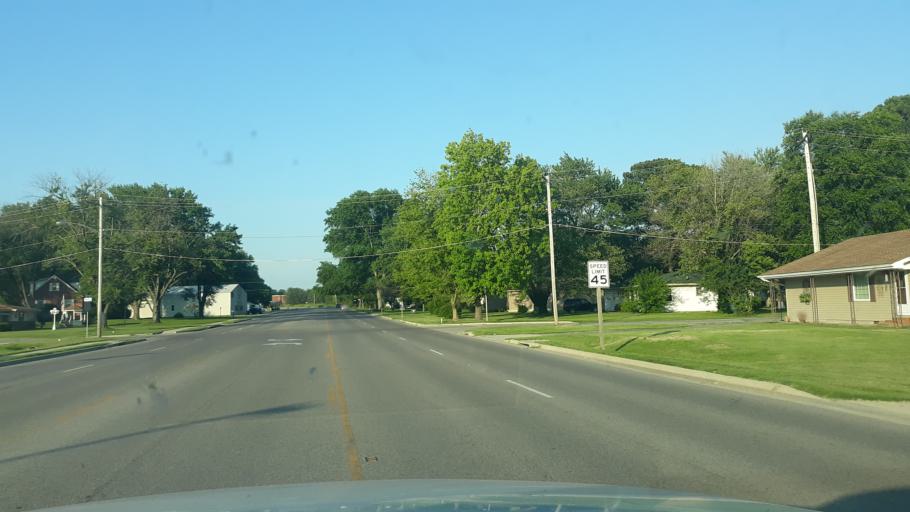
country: US
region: Illinois
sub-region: Saline County
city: Eldorado
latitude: 37.8093
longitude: -88.4325
